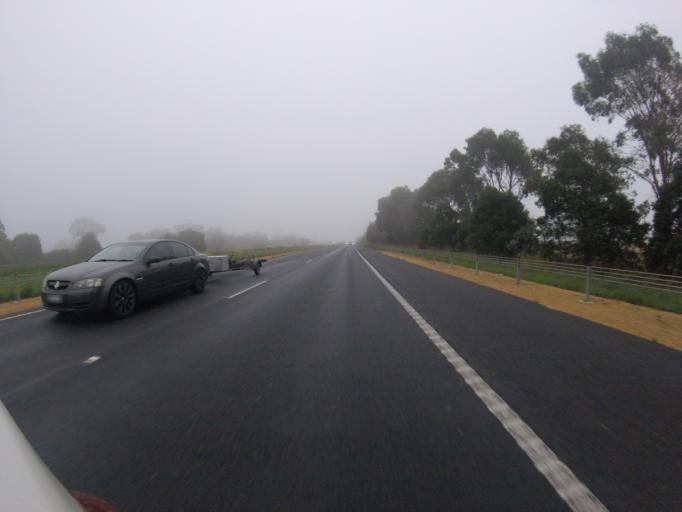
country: AU
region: Victoria
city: Brown Hill
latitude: -37.5911
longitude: 144.1719
